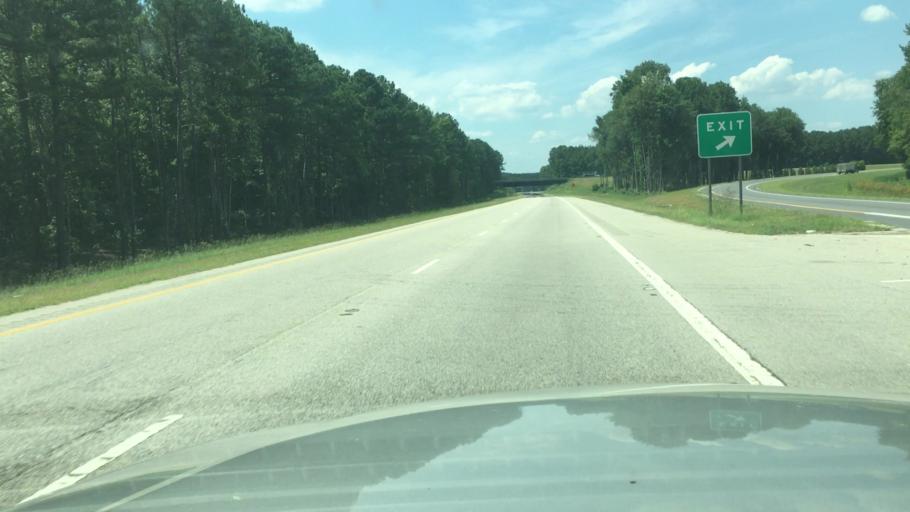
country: US
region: North Carolina
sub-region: Cumberland County
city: Vander
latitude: 34.9728
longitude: -78.8531
